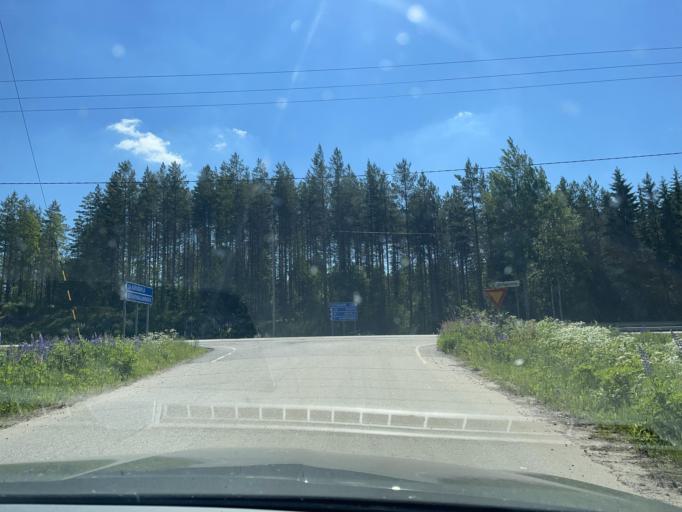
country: FI
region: Central Finland
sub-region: Saarijaervi-Viitasaari
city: Viitasaari
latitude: 63.1785
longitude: 26.0327
